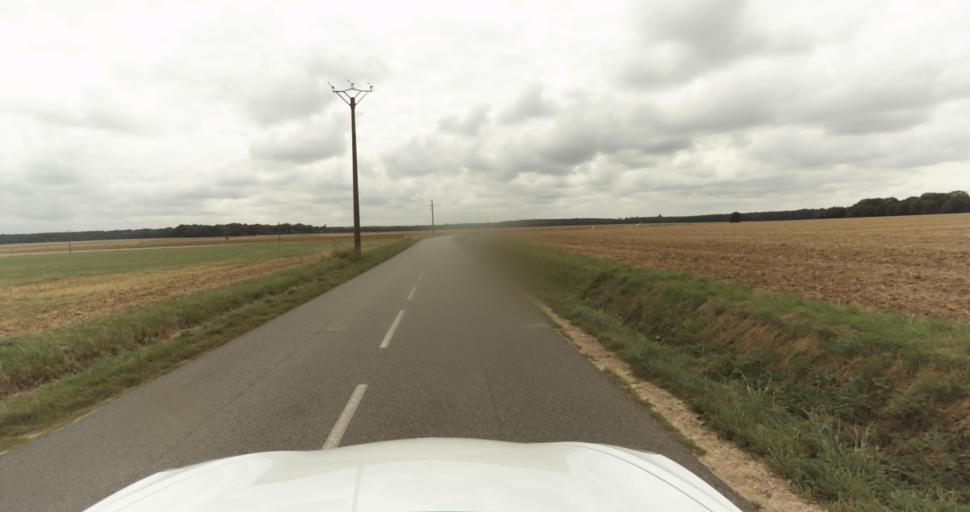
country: FR
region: Haute-Normandie
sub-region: Departement de l'Eure
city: Claville
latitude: 49.0189
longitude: 1.0336
